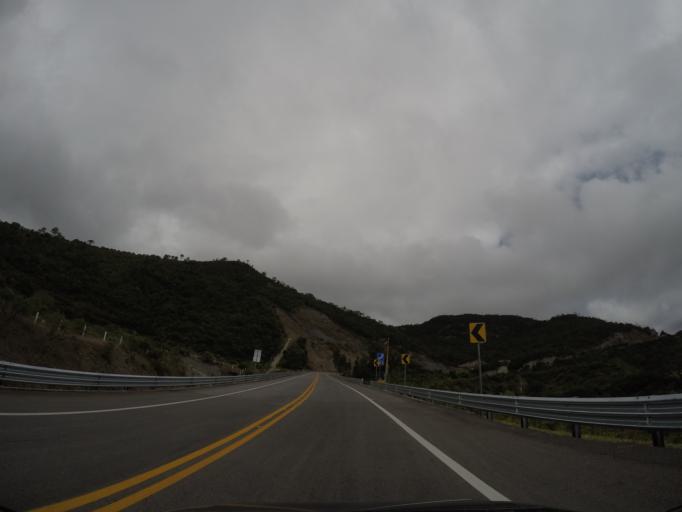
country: MX
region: Oaxaca
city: San Lorenzo Albarradas
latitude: 16.9372
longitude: -96.2699
